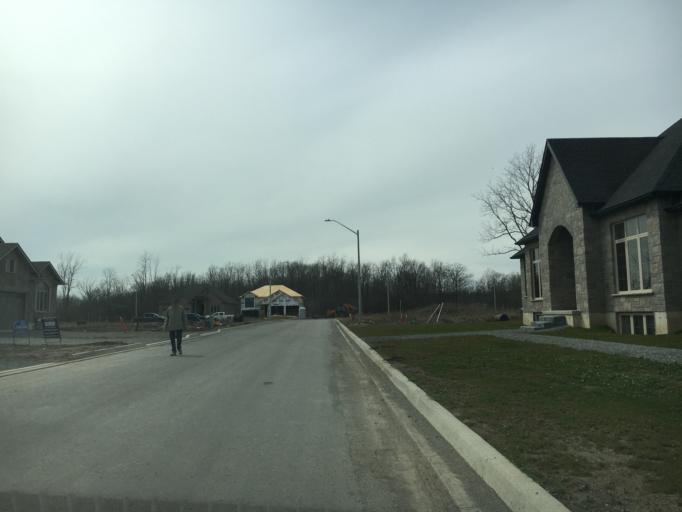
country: CA
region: Ontario
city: Port Colborne
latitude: 42.8833
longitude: -79.2783
